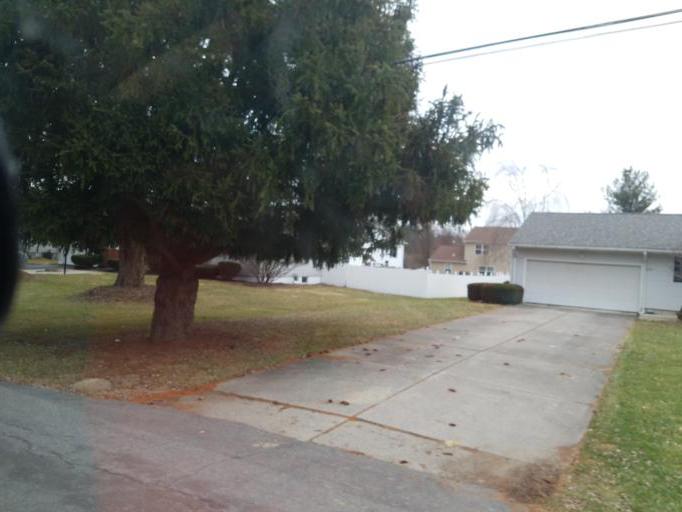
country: US
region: Ohio
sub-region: Marion County
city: Marion
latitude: 40.5689
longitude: -83.0861
